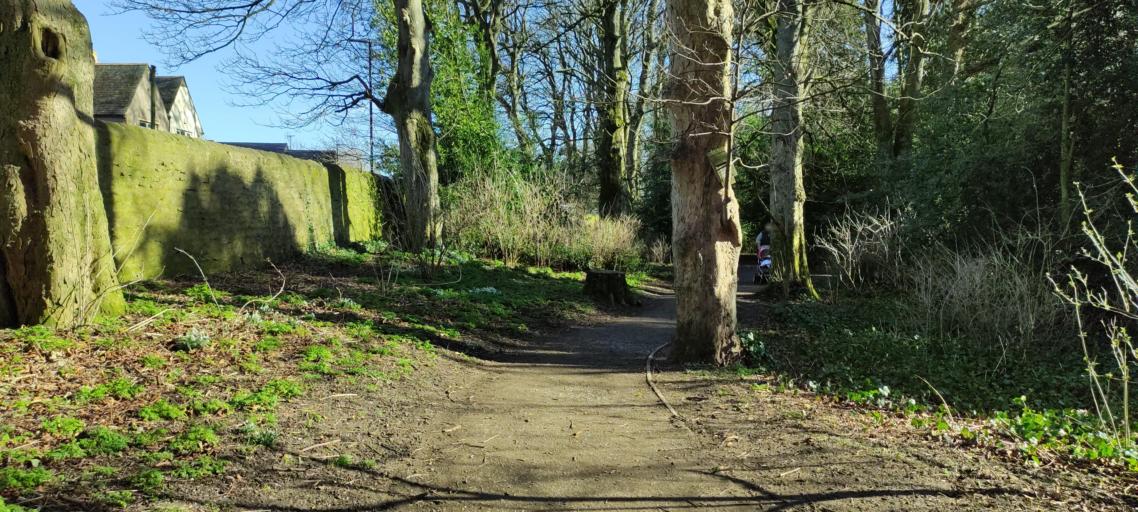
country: GB
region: England
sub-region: County Durham
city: Barnard Castle
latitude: 54.5435
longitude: -1.9165
